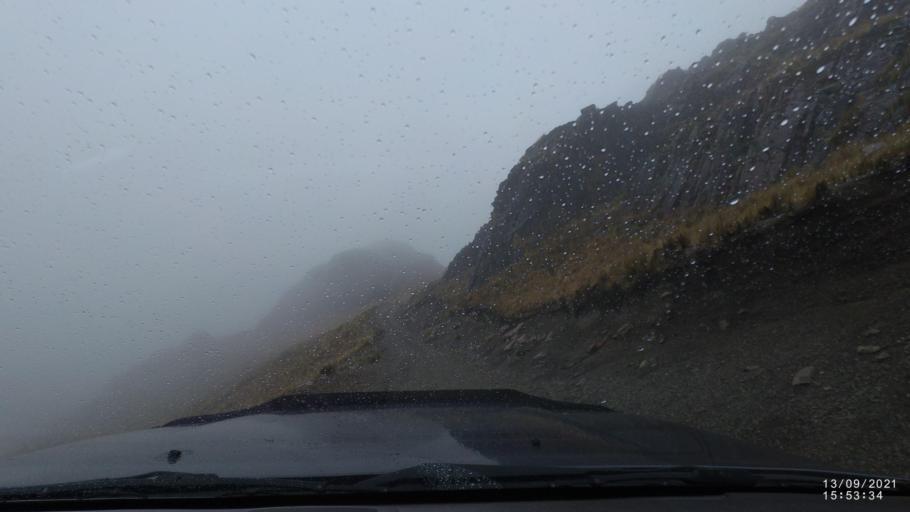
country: BO
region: Cochabamba
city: Colomi
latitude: -17.3053
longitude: -65.7094
